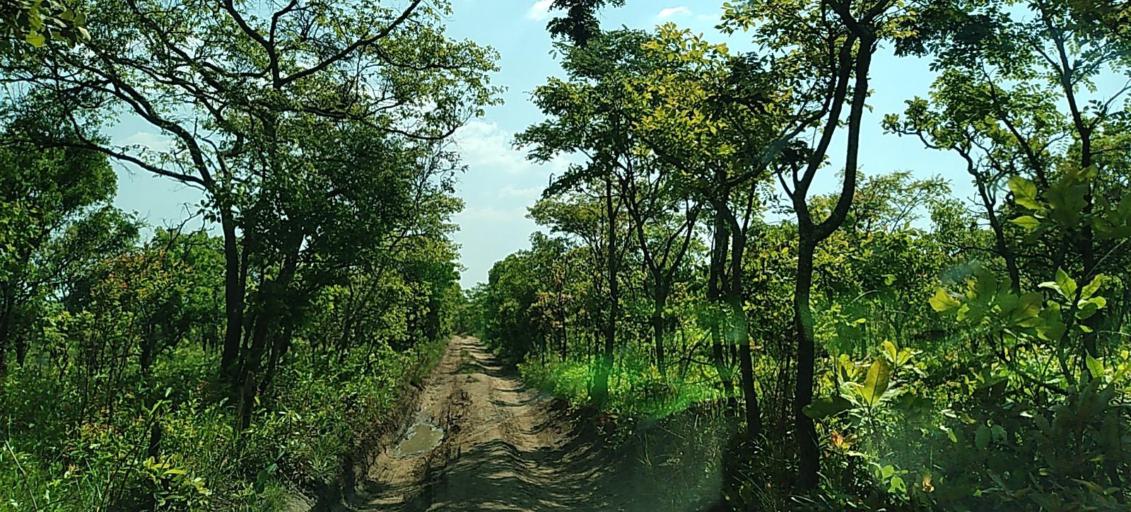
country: CD
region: Katanga
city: Kolwezi
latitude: -11.2645
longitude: 25.0020
